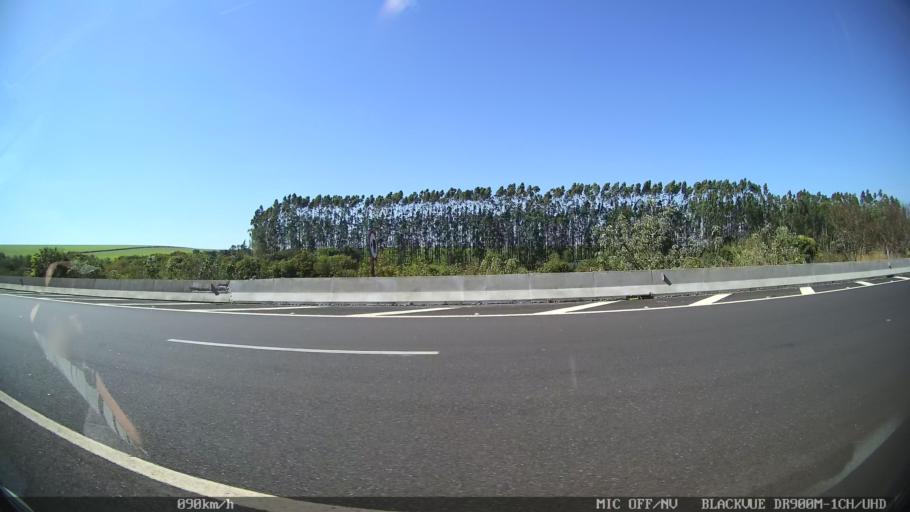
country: BR
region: Sao Paulo
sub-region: Franca
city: Franca
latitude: -20.6901
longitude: -47.4974
